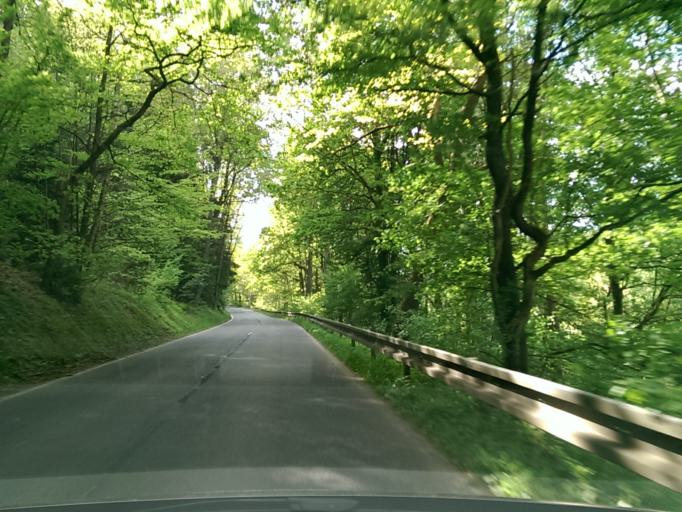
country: CZ
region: Central Bohemia
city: Bakov nad Jizerou
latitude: 50.4956
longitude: 14.8998
